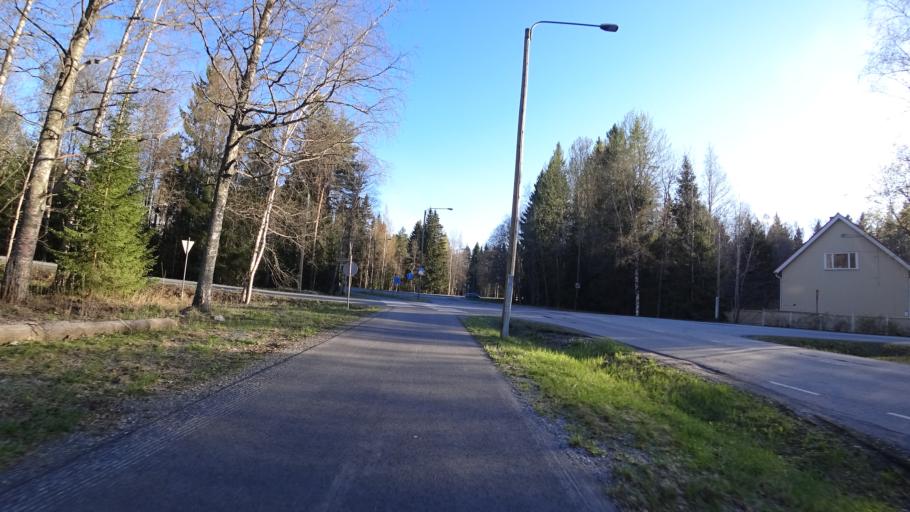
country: FI
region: Pirkanmaa
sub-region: Tampere
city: Yloejaervi
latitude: 61.5049
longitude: 23.5923
